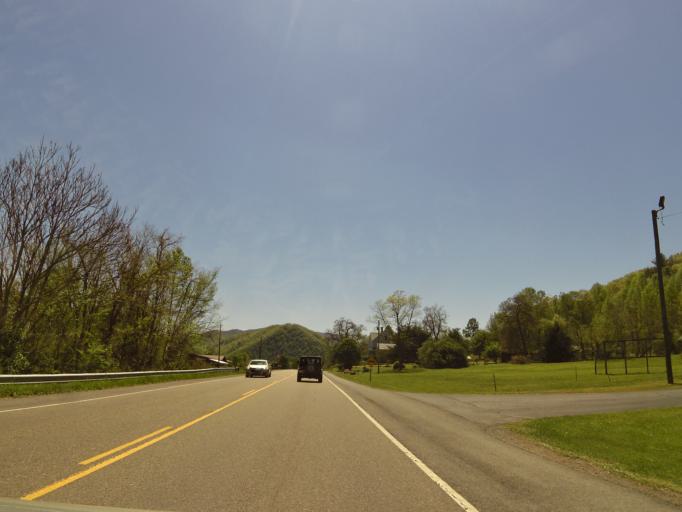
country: US
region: Tennessee
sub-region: Unicoi County
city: Erwin
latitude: 36.1844
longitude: -82.4565
